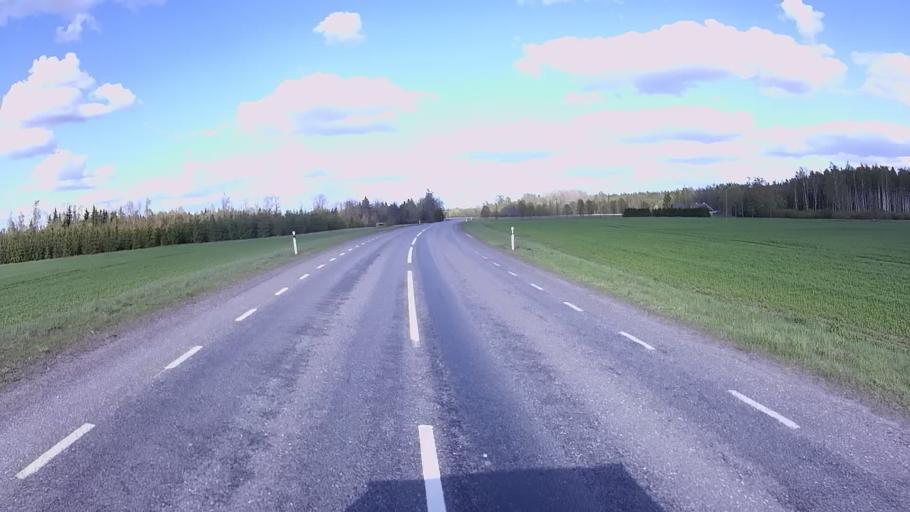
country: EE
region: Jogevamaa
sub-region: Poltsamaa linn
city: Poltsamaa
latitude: 58.7009
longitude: 26.1473
